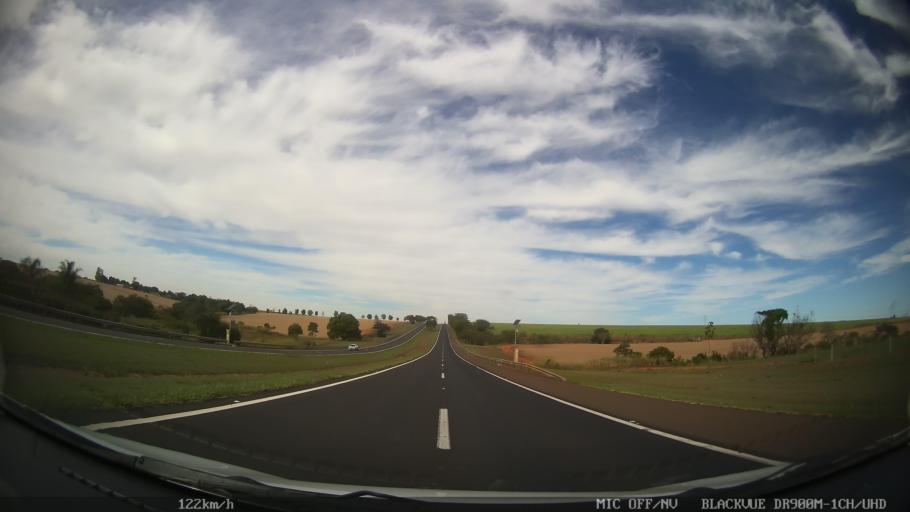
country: BR
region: Sao Paulo
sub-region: Taquaritinga
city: Taquaritinga
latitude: -21.5075
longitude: -48.5527
